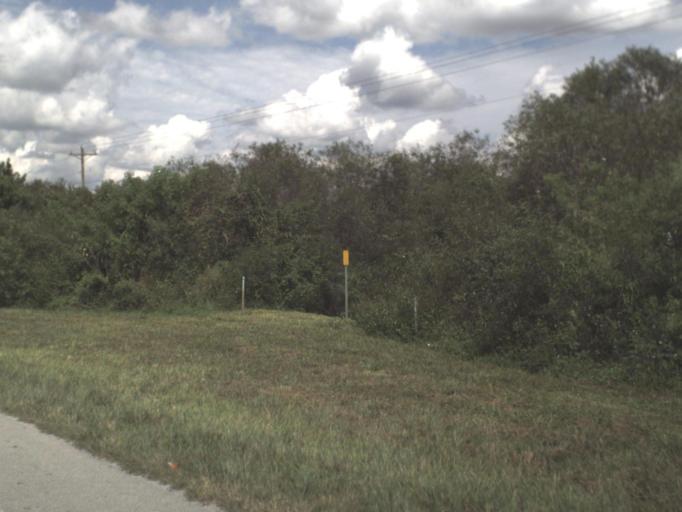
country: US
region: Florida
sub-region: Collier County
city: Immokalee
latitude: 26.4797
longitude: -81.4346
